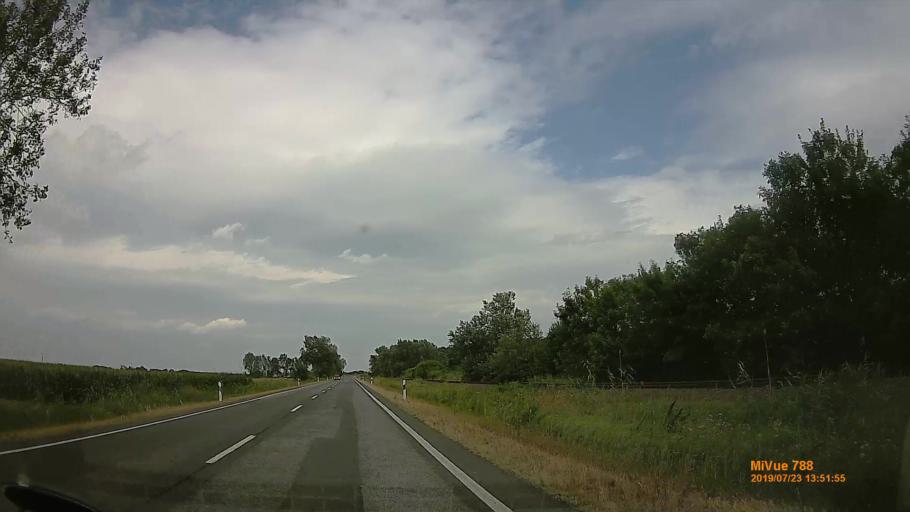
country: HU
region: Hajdu-Bihar
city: Polgar
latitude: 47.8953
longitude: 21.1550
